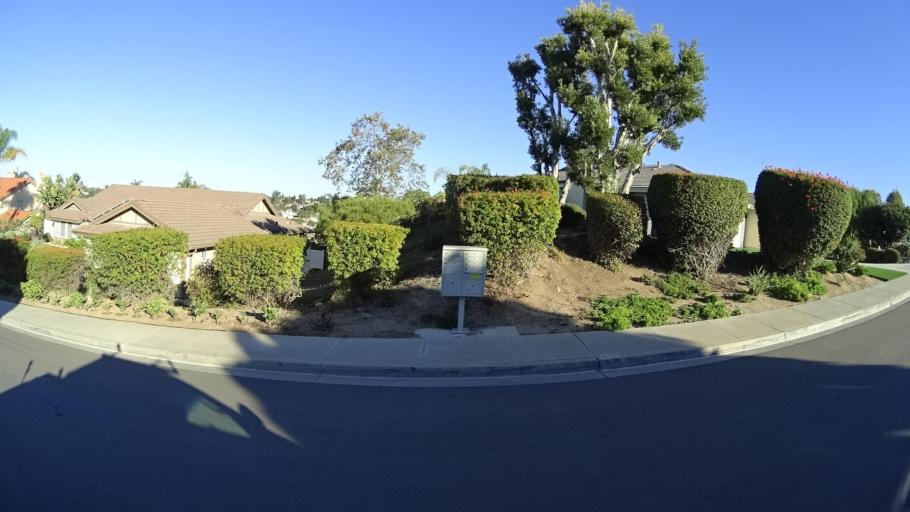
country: US
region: California
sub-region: San Diego County
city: Bonita
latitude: 32.6728
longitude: -117.0368
